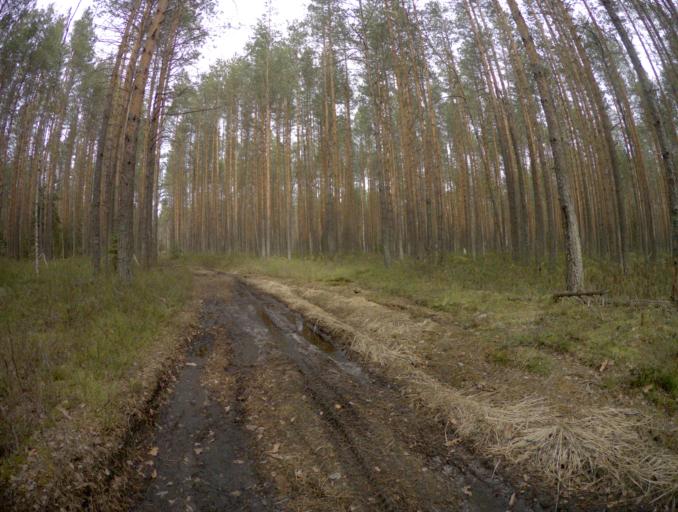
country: RU
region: Vladimir
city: Raduzhnyy
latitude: 55.9330
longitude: 40.2810
